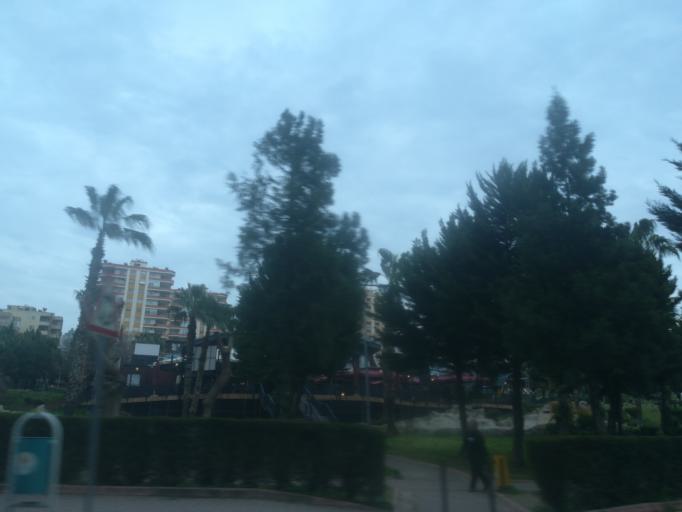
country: TR
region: Adana
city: Adana
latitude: 37.0375
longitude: 35.2938
